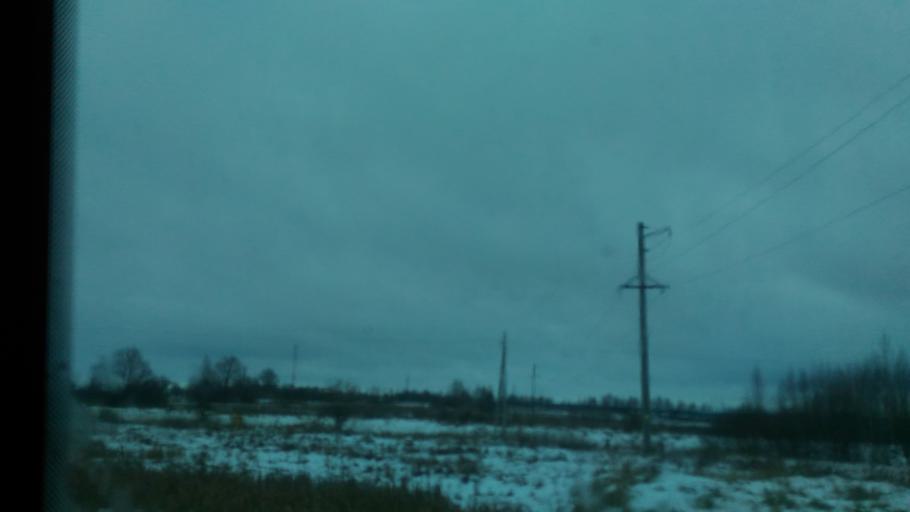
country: RU
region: Tula
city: Bolokhovo
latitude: 54.0602
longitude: 37.8039
